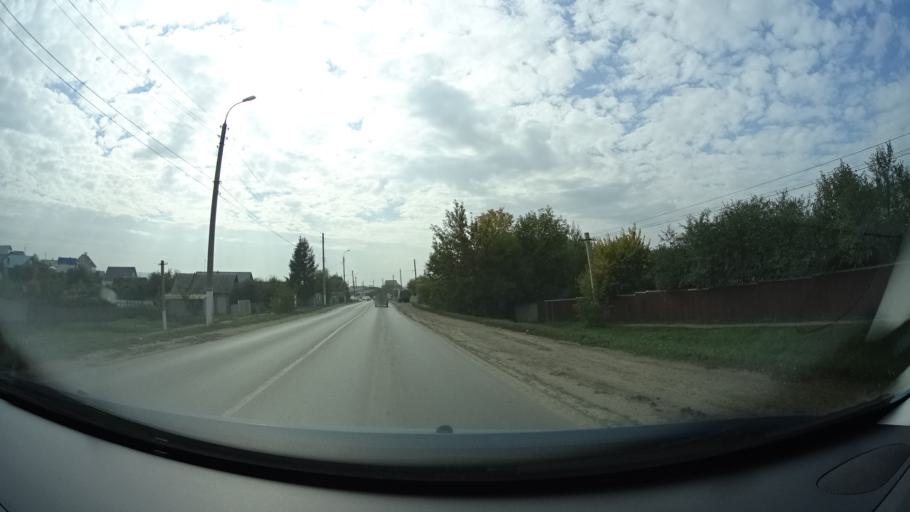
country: RU
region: Bashkortostan
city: Oktyabr'skiy
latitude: 54.5121
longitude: 53.5179
